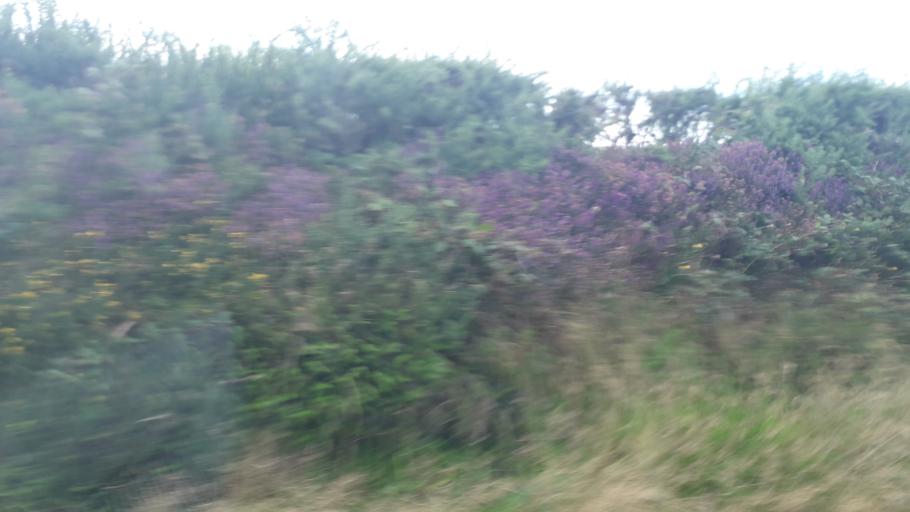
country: GB
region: Northern Ireland
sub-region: Down District
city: Warrenpoint
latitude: 54.0405
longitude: -6.2670
